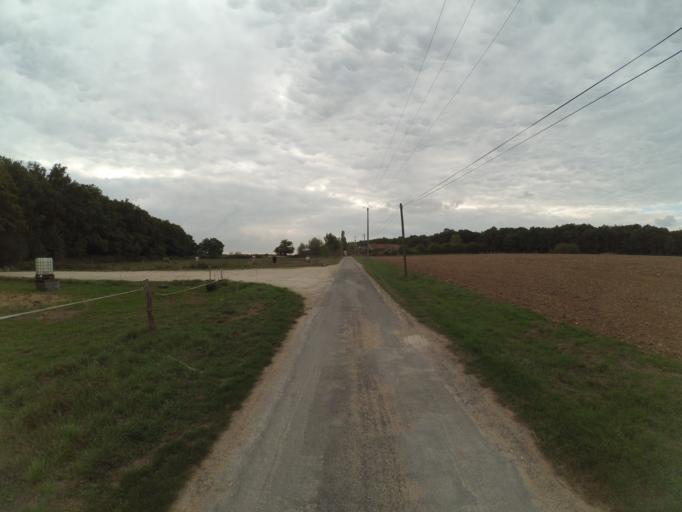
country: FR
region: Centre
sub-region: Departement d'Indre-et-Loire
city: Reugny
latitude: 47.4940
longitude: 0.9252
